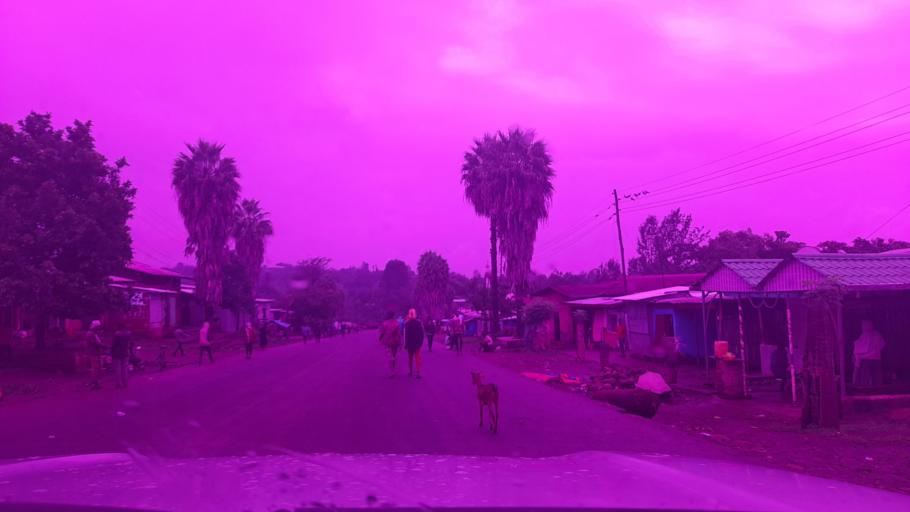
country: ET
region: Oromiya
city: Jima
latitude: 7.8421
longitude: 37.3672
